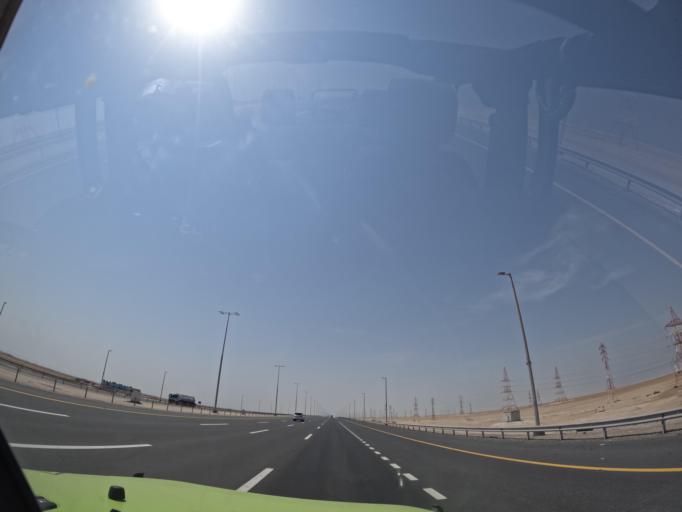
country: AE
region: Abu Dhabi
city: Abu Dhabi
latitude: 24.1568
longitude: 54.3027
